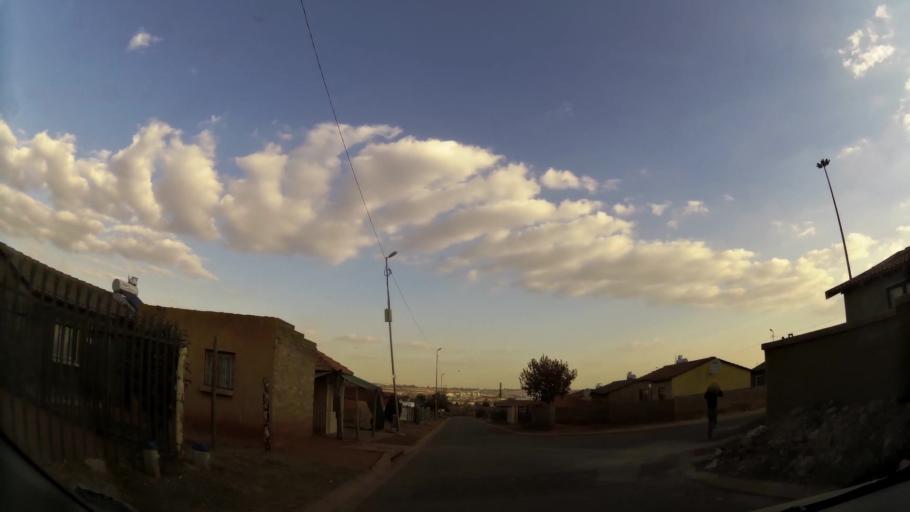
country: ZA
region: Gauteng
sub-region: West Rand District Municipality
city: Krugersdorp
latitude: -26.0780
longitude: 27.7598
